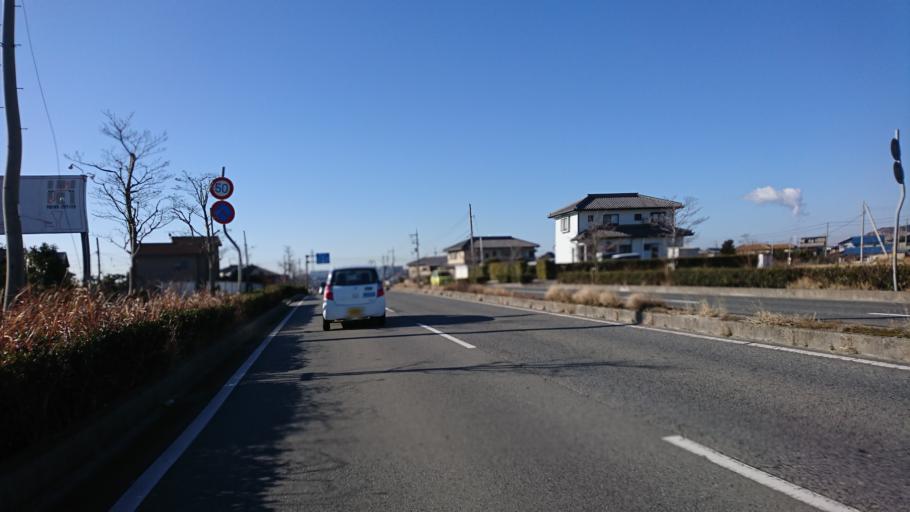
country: JP
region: Hyogo
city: Kakogawacho-honmachi
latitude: 34.7961
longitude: 134.8268
